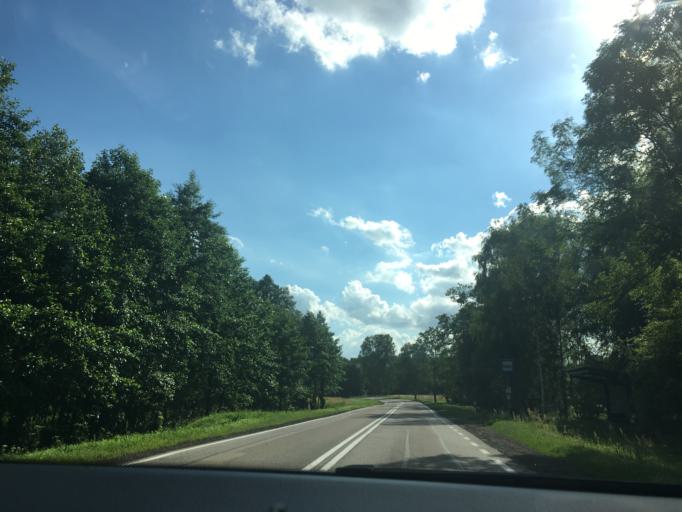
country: PL
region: Podlasie
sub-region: Powiat bialostocki
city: Zabludow
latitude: 52.9603
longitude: 23.2788
